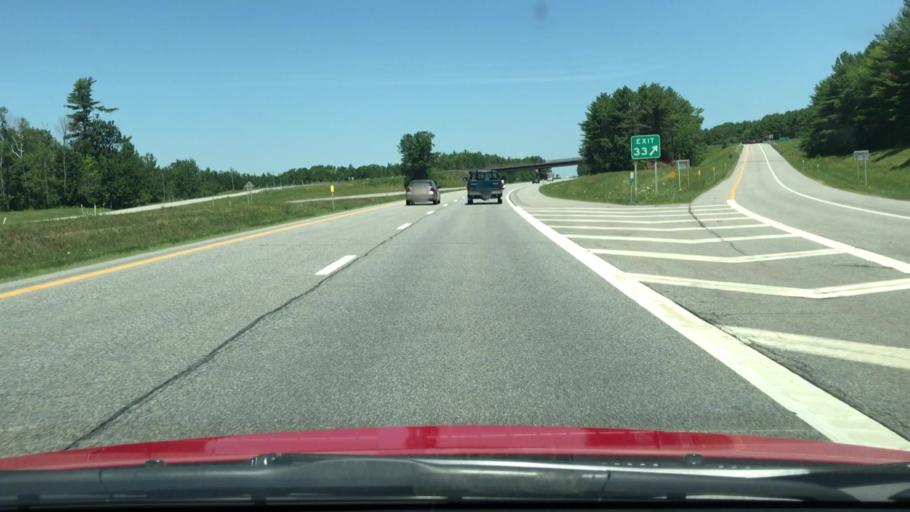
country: US
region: New York
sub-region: Essex County
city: Keeseville
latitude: 44.4407
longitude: -73.4919
